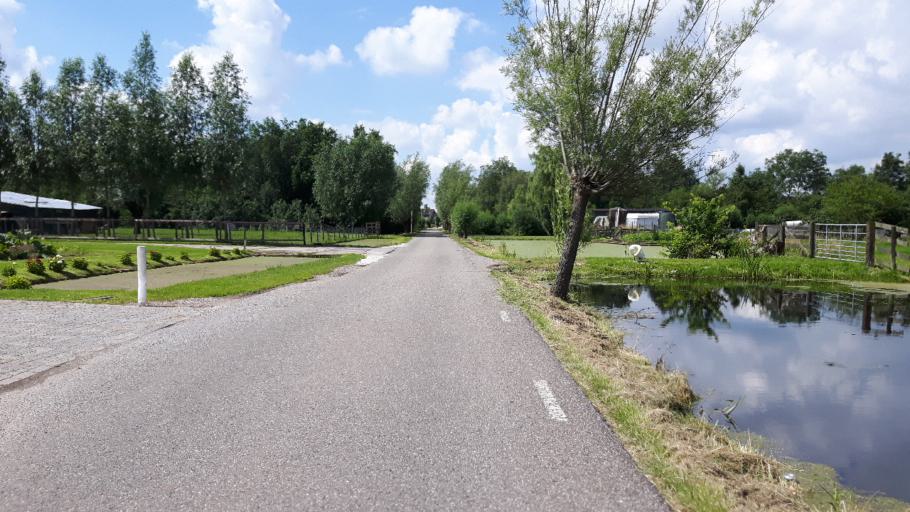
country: NL
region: Utrecht
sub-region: Gemeente Oudewater
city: Oudewater
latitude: 52.0596
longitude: 4.8275
